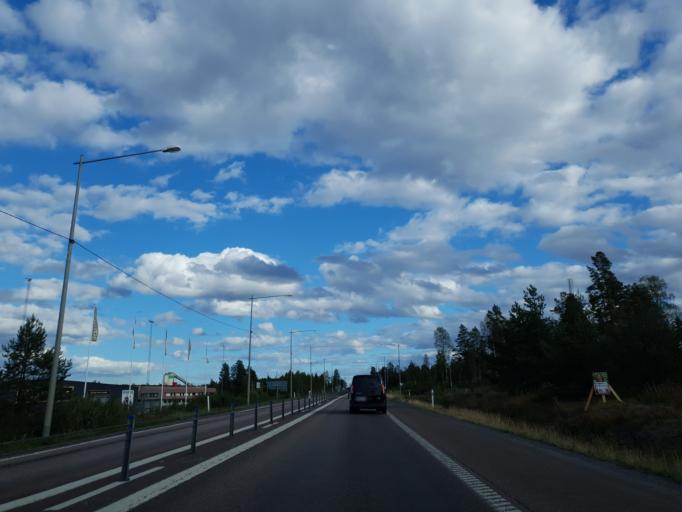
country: SE
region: Vaesternorrland
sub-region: Haernoesands Kommun
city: Haernoesand
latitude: 62.6532
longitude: 17.8847
